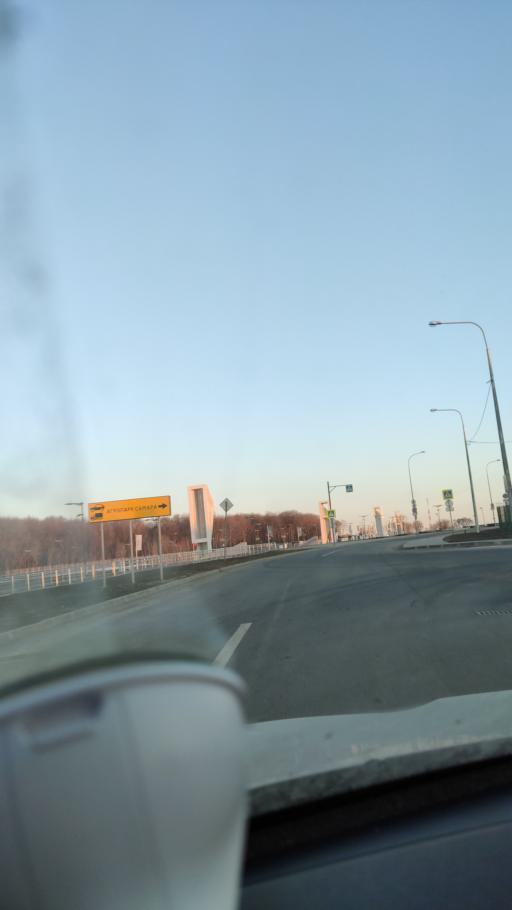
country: RU
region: Samara
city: Petra-Dubrava
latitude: 53.2738
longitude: 50.2542
